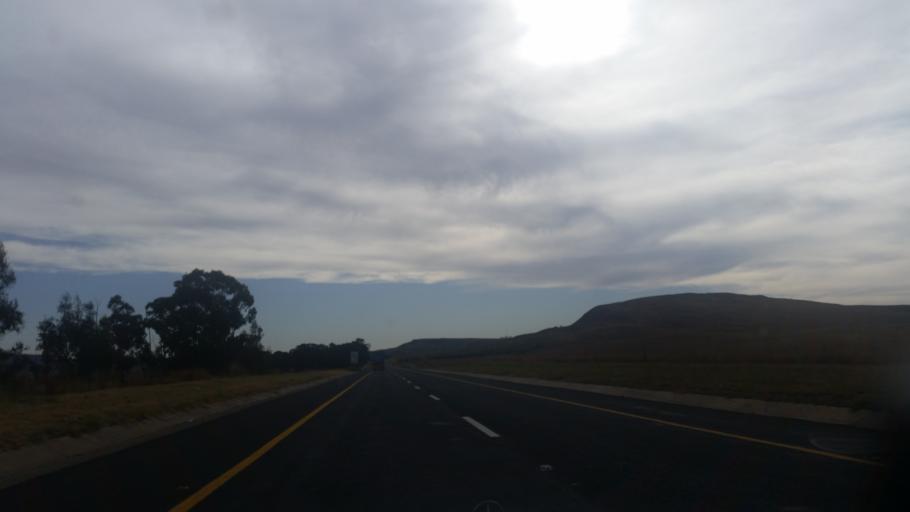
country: ZA
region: Orange Free State
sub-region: Thabo Mofutsanyana District Municipality
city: Phuthaditjhaba
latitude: -28.3131
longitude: 28.7350
